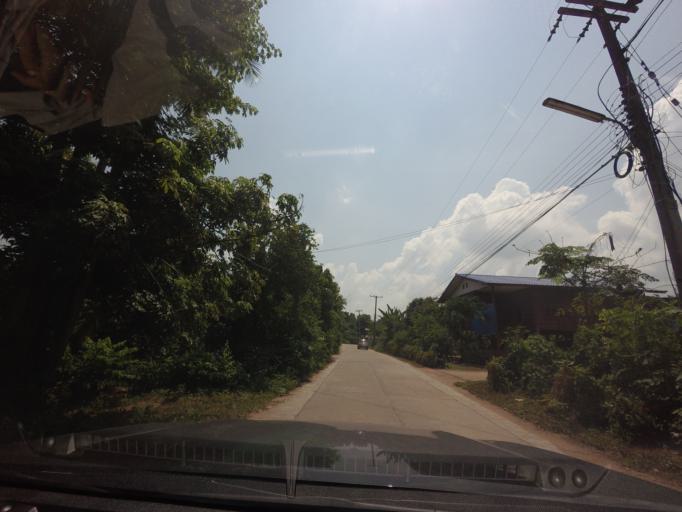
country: TH
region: Uttaradit
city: Thong Saen Khan
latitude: 17.4586
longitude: 100.3082
